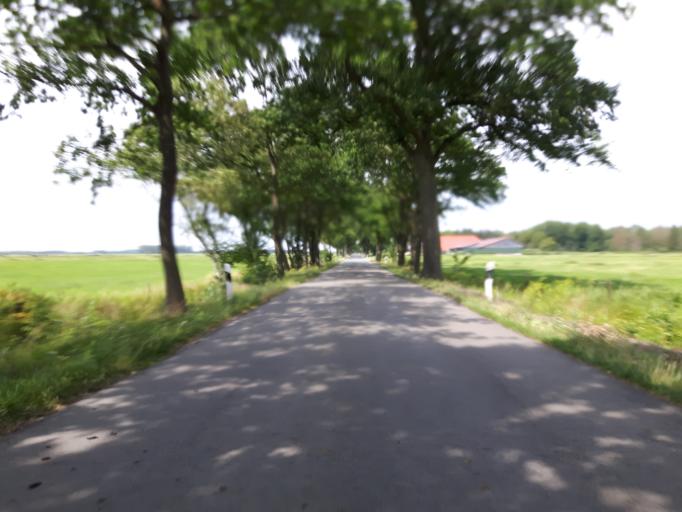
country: DE
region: Lower Saxony
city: Rastede
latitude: 53.3264
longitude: 8.2776
